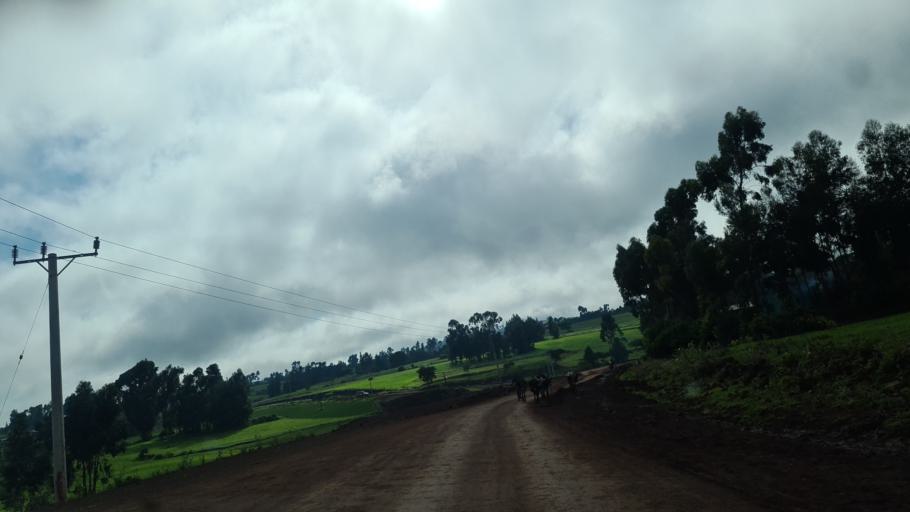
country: ET
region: Oromiya
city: Huruta
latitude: 8.1252
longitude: 39.3731
